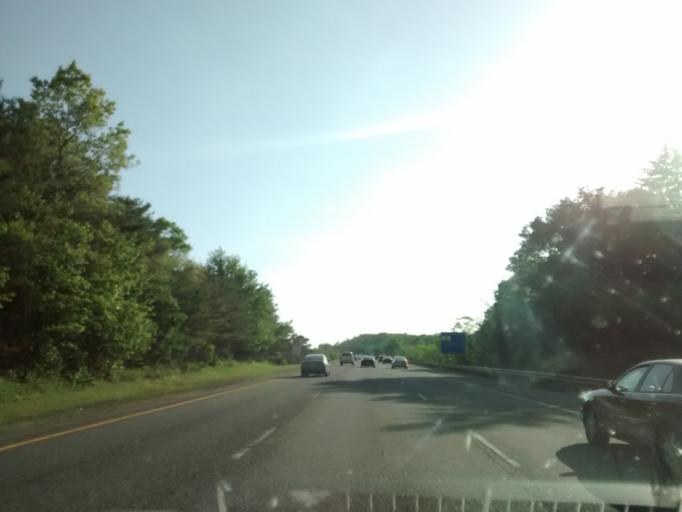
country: US
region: Massachusetts
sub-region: Worcester County
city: Shrewsbury
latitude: 42.3244
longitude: -71.7105
